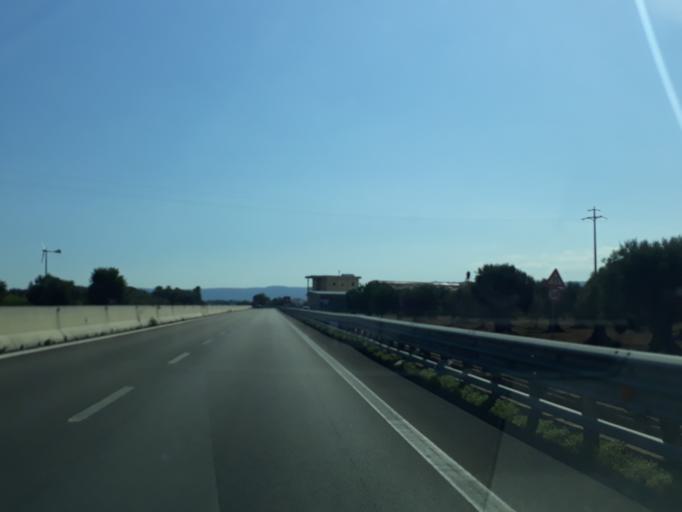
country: IT
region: Apulia
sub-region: Provincia di Brindisi
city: Fasano
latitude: 40.8619
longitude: 17.3478
